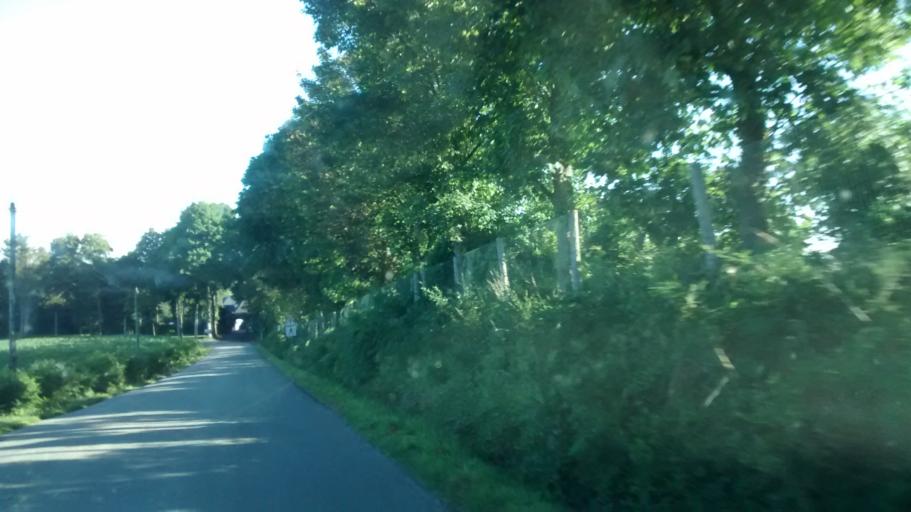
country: FR
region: Brittany
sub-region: Departement du Morbihan
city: Campeneac
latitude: 47.9760
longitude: -2.3065
